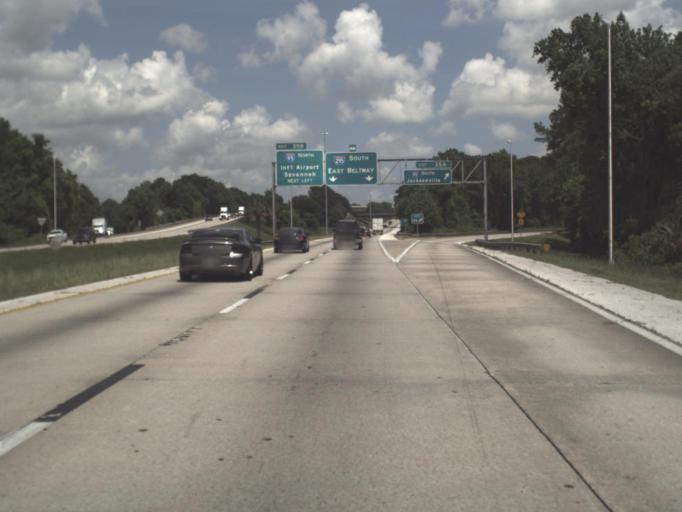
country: US
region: Florida
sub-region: Duval County
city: Jacksonville
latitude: 30.4598
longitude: -81.6564
